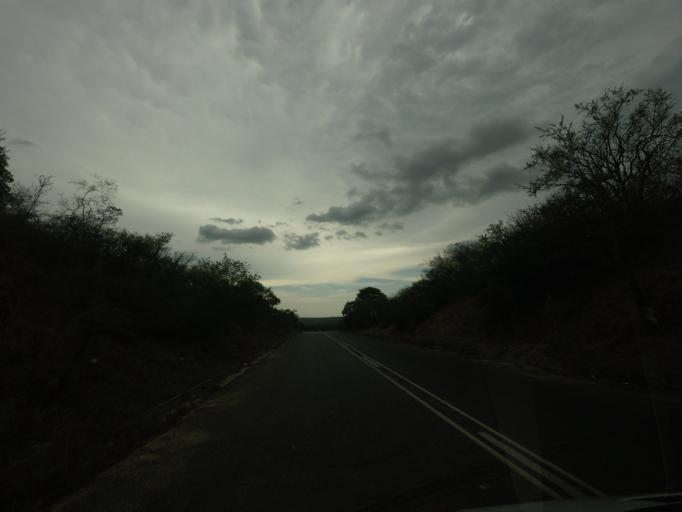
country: ZA
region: Limpopo
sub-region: Mopani District Municipality
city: Hoedspruit
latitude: -24.5402
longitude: 31.0287
